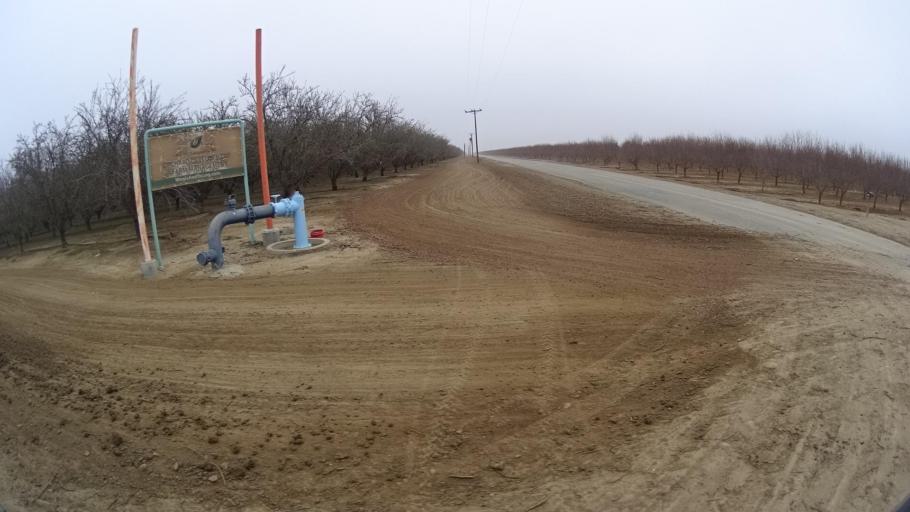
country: US
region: California
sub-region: Kern County
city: Wasco
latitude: 35.5722
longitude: -119.5096
